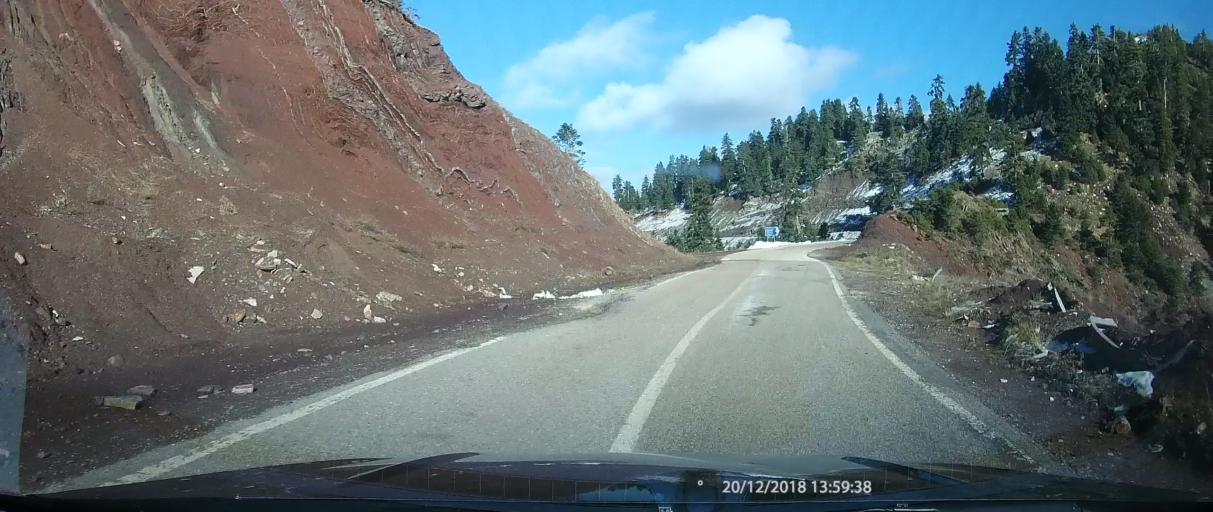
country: GR
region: West Greece
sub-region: Nomos Aitolias kai Akarnanias
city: Thermo
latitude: 38.7197
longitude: 21.6251
